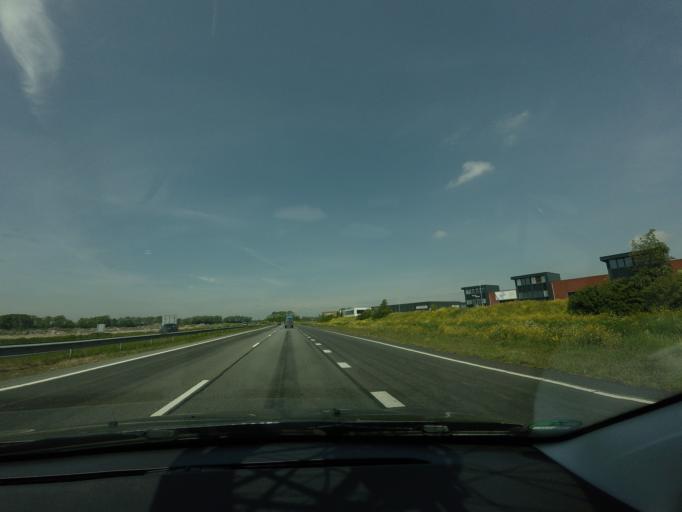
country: NL
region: Friesland
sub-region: Sudwest Fryslan
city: IJlst
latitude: 53.0364
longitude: 5.6200
